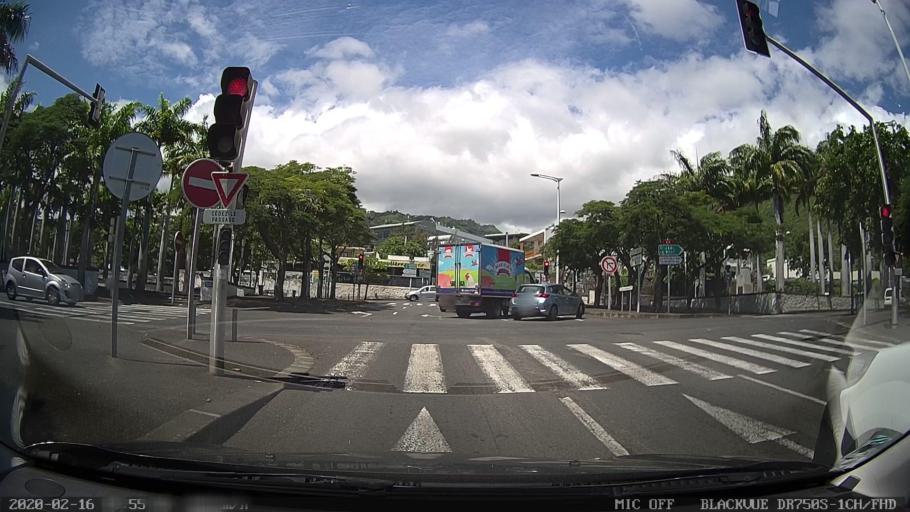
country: RE
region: Reunion
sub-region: Reunion
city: Saint-Denis
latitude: -20.8879
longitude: 55.4443
